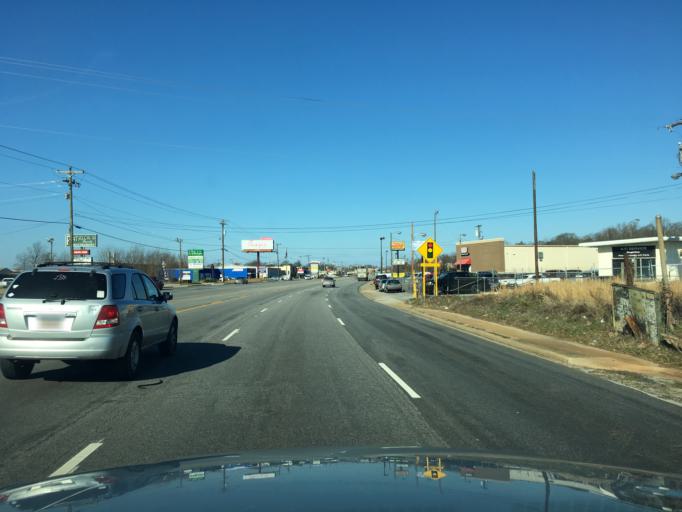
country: US
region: South Carolina
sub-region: Greenville County
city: Sans Souci
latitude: 34.8873
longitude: -82.3957
